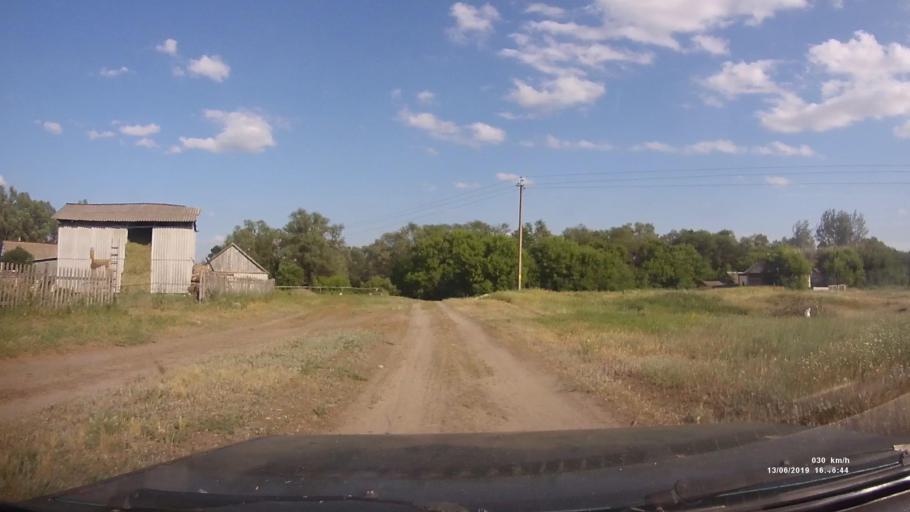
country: RU
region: Rostov
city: Kazanskaya
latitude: 49.9448
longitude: 41.4289
